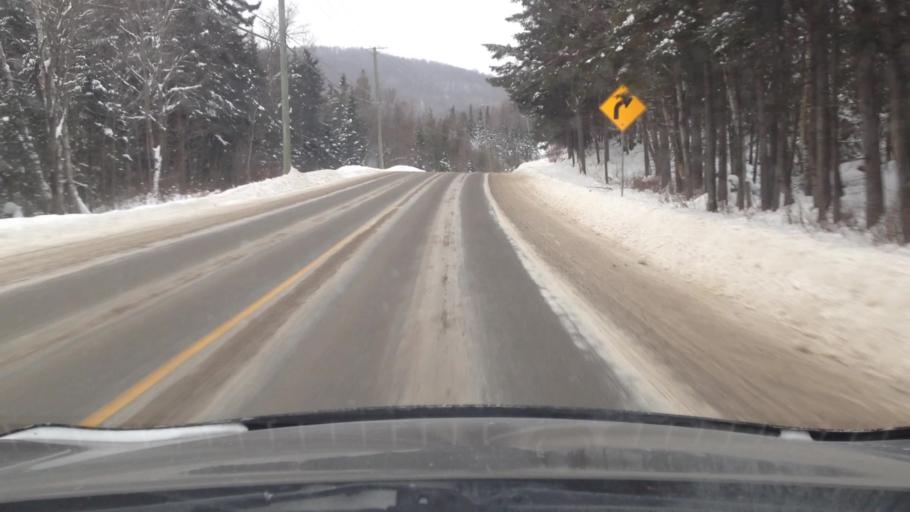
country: CA
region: Quebec
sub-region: Laurentides
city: Saint-Sauveur
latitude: 45.9072
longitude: -74.2967
